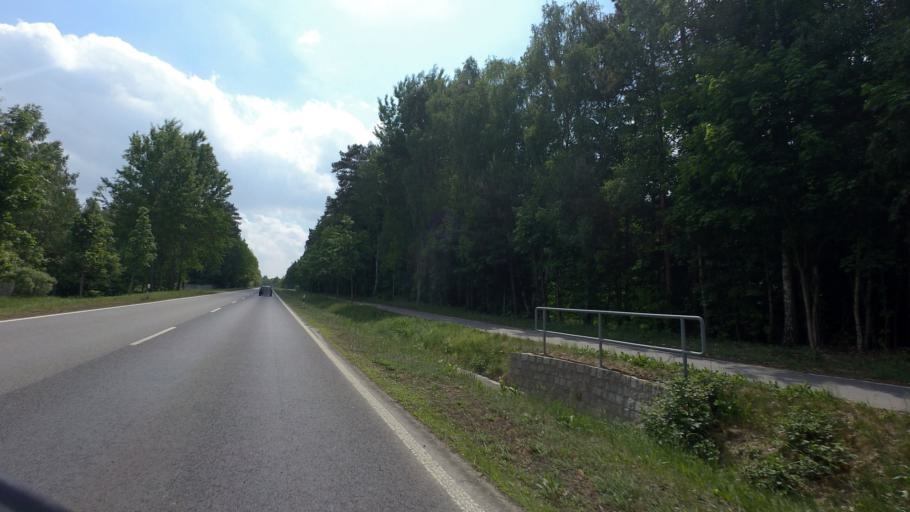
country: DE
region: Saxony
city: Weisskeissel
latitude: 51.4807
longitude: 14.7226
